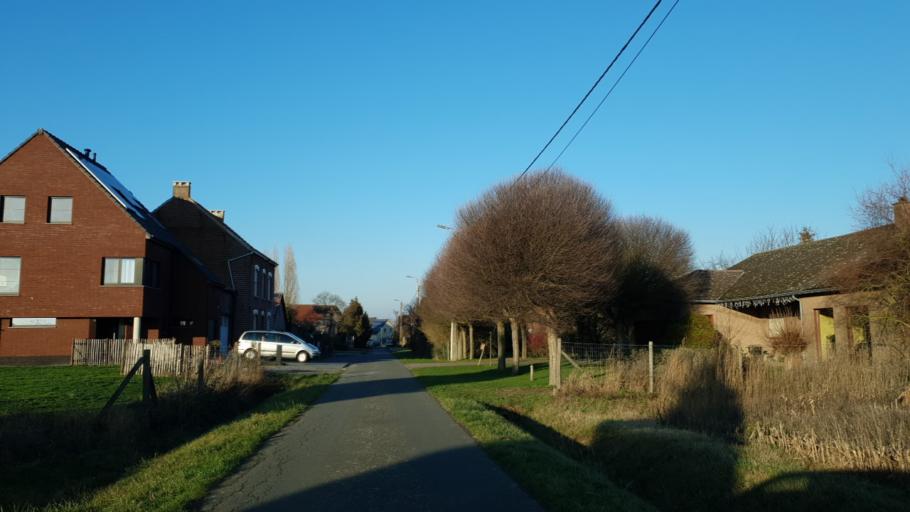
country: BE
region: Flanders
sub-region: Provincie Vlaams-Brabant
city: Herent
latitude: 50.9363
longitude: 4.6506
